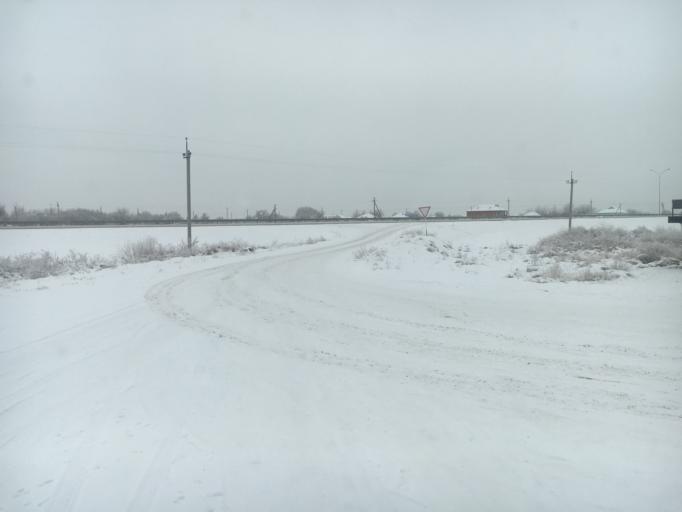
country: KZ
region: Qyzylorda
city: Tasboget
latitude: 44.7660
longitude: 65.5058
